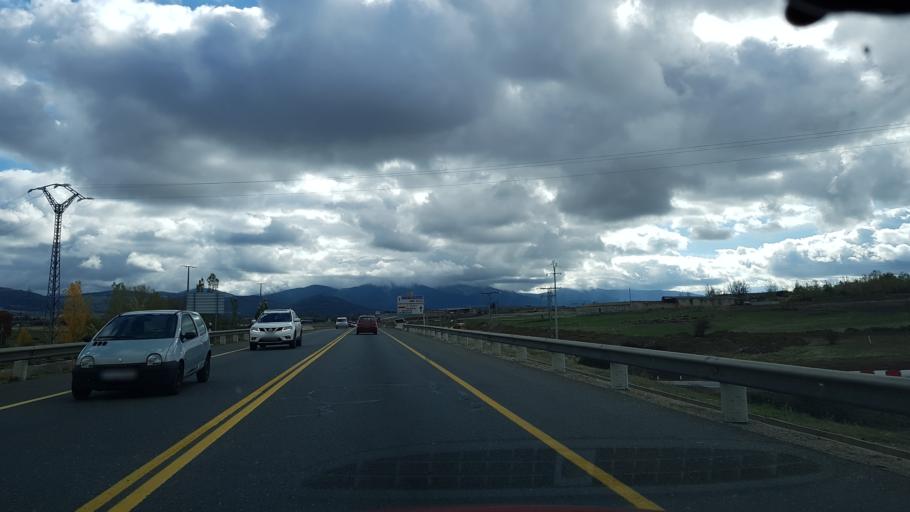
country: ES
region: Castille and Leon
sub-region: Provincia de Segovia
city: San Cristobal de Segovia
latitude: 40.9372
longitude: -4.0858
